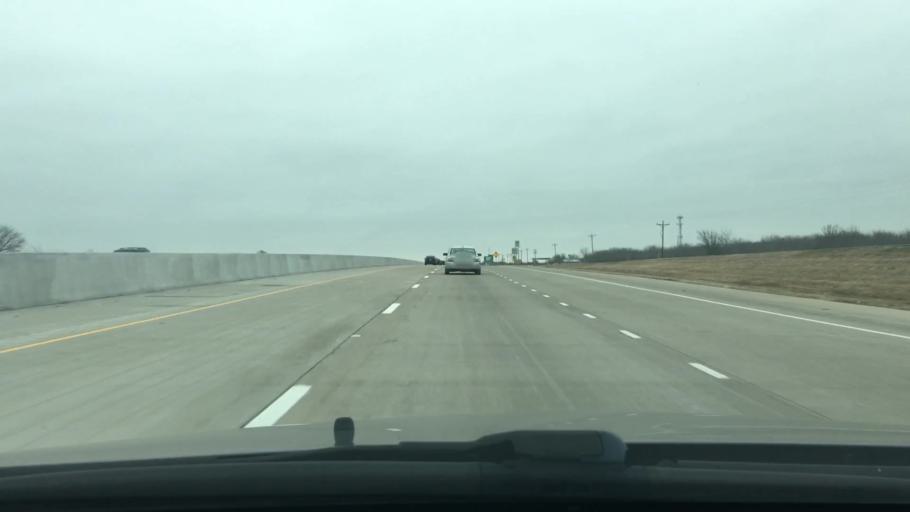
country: US
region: Texas
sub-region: Freestone County
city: Wortham
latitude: 31.8857
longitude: -96.3511
